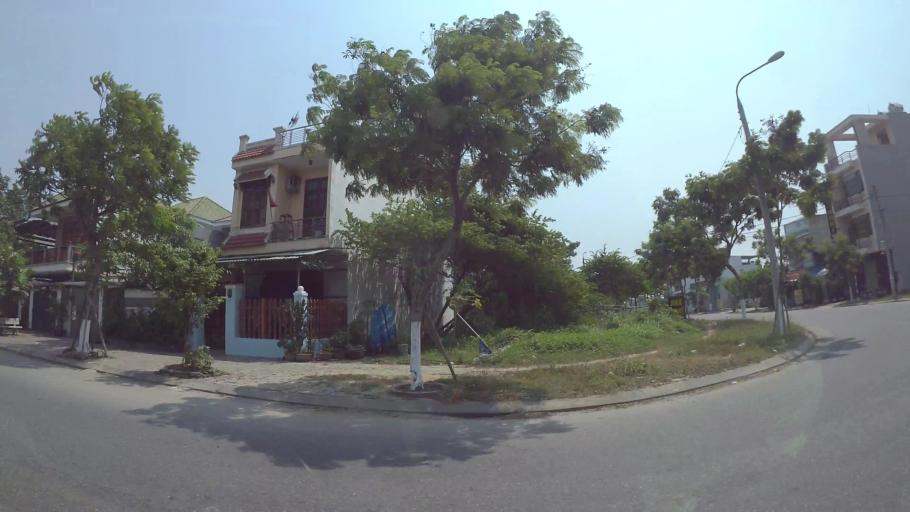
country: VN
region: Da Nang
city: Cam Le
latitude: 15.9973
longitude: 108.1968
